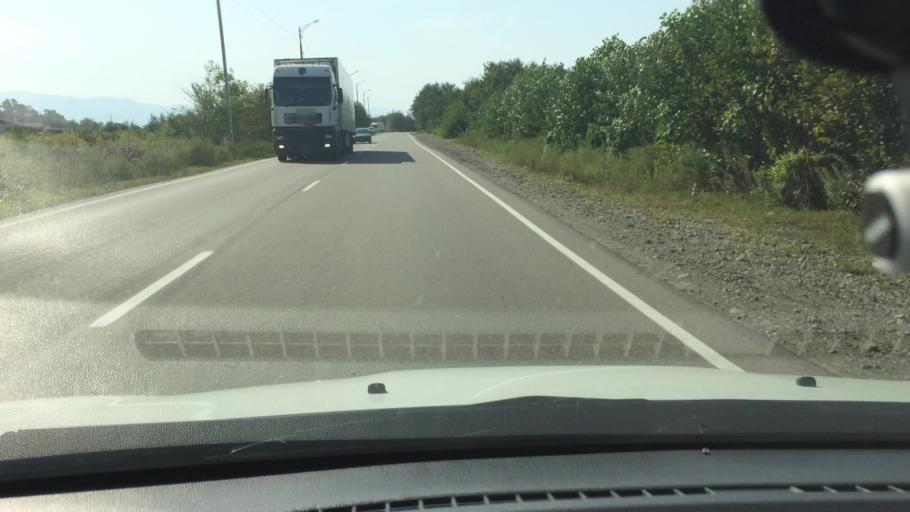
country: GE
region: Guria
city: Urek'i
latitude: 41.9624
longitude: 41.7730
